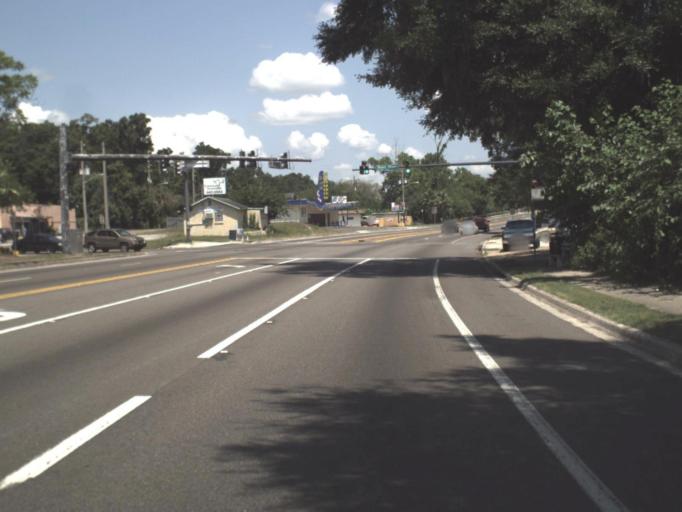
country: US
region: Florida
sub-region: Duval County
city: Jacksonville
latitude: 30.4151
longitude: -81.6948
